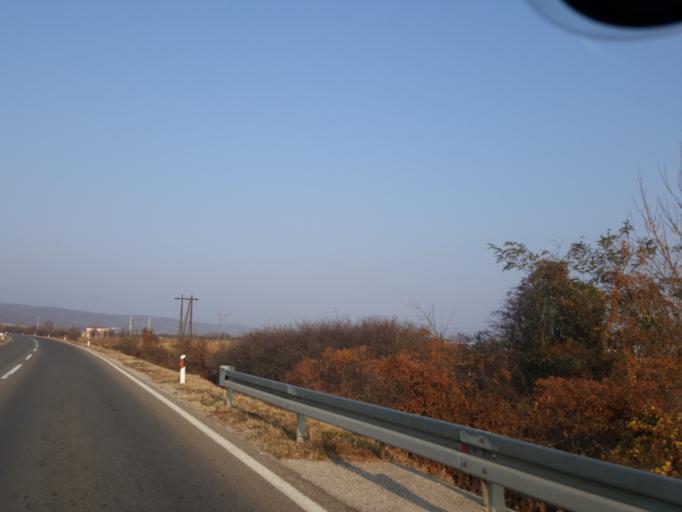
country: RS
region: Central Serbia
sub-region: Jablanicki Okrug
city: Leskovac
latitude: 42.9362
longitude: 22.0079
